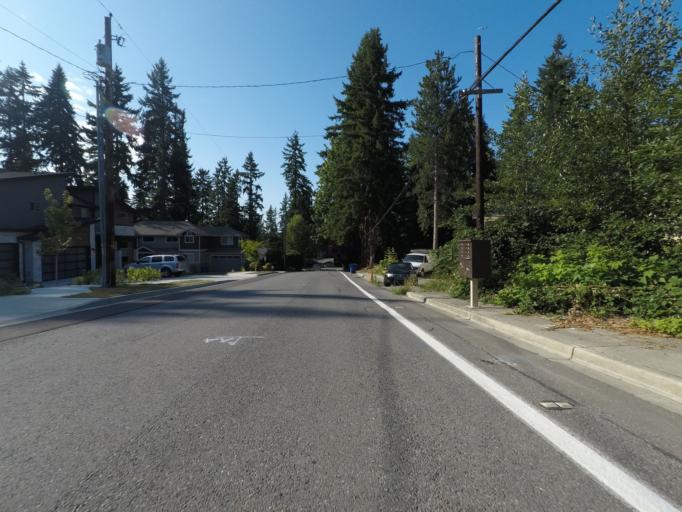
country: US
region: Washington
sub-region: King County
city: Kenmore
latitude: 47.7469
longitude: -122.2353
